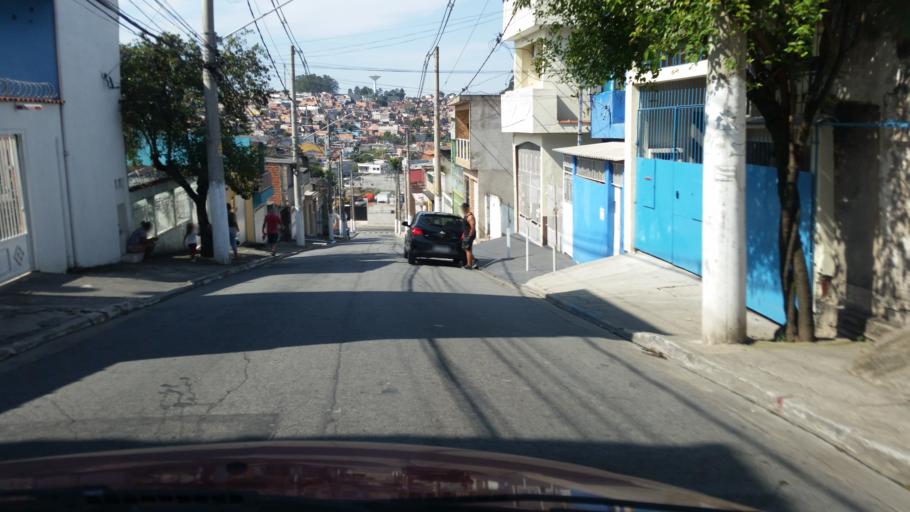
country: BR
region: Sao Paulo
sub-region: Ferraz De Vasconcelos
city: Ferraz de Vasconcelos
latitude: -23.5625
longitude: -46.4207
